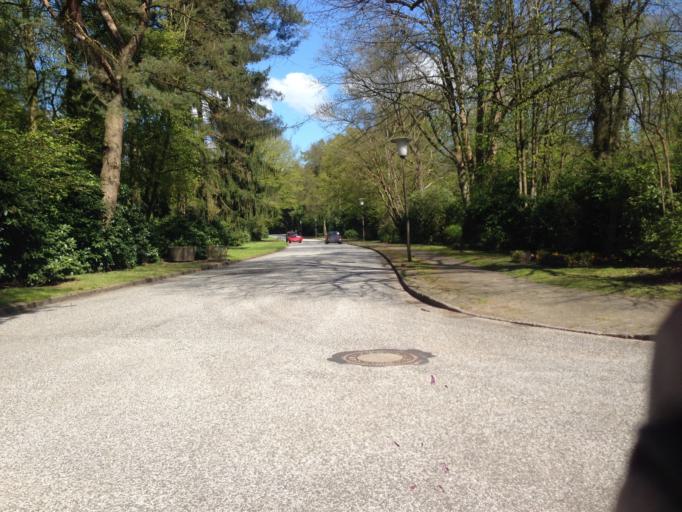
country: DE
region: Hamburg
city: Barmbek-Nord
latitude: 53.6180
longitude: 10.0463
